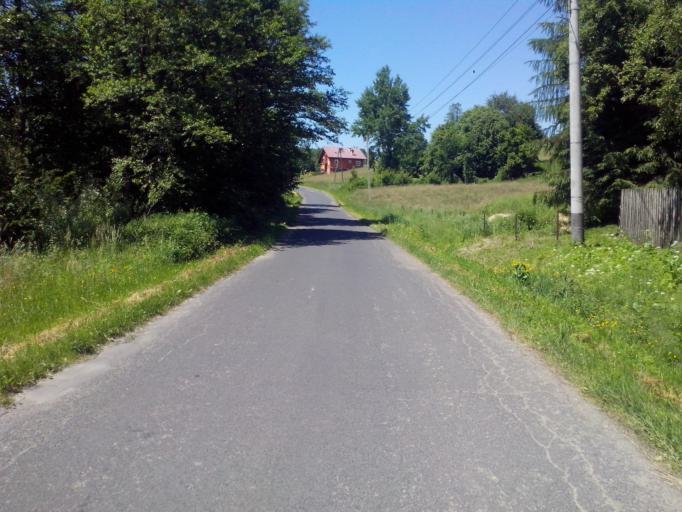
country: PL
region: Subcarpathian Voivodeship
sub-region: Powiat krosnienski
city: Leki
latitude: 49.8052
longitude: 21.6930
